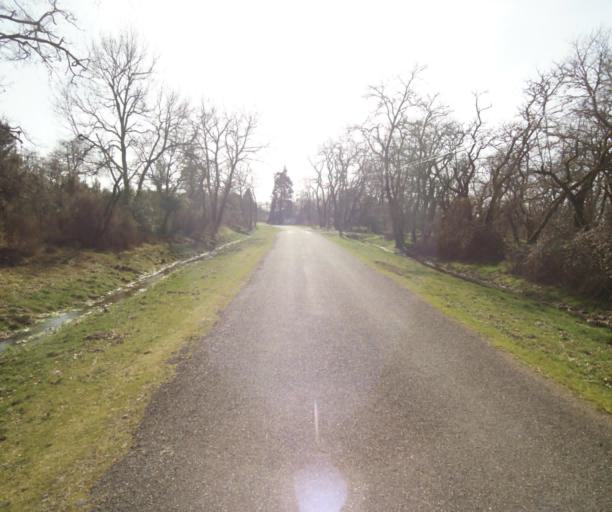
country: FR
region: Aquitaine
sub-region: Departement des Landes
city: Roquefort
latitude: 44.1286
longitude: -0.1917
